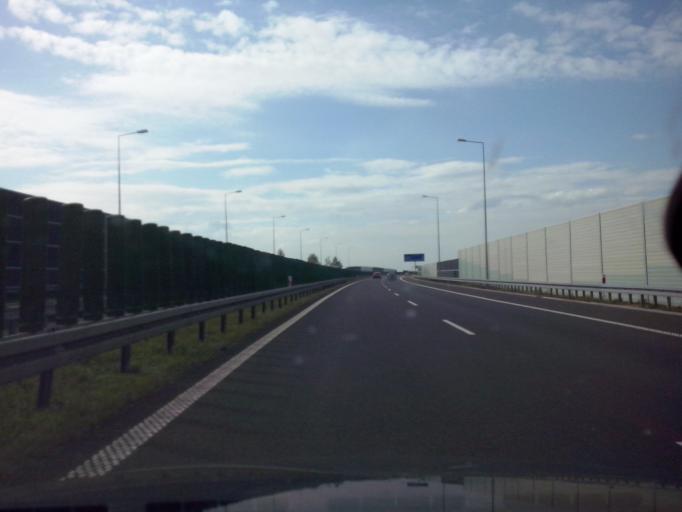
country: PL
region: Lesser Poland Voivodeship
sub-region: Powiat tarnowski
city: Lisia Gora
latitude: 50.0544
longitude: 21.0089
